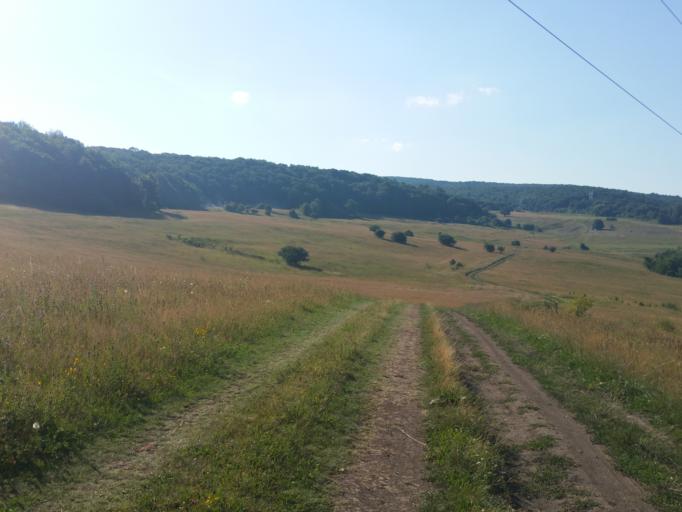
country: RO
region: Cluj
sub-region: Comuna Baciu
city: Baciu
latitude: 46.8053
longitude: 23.5286
